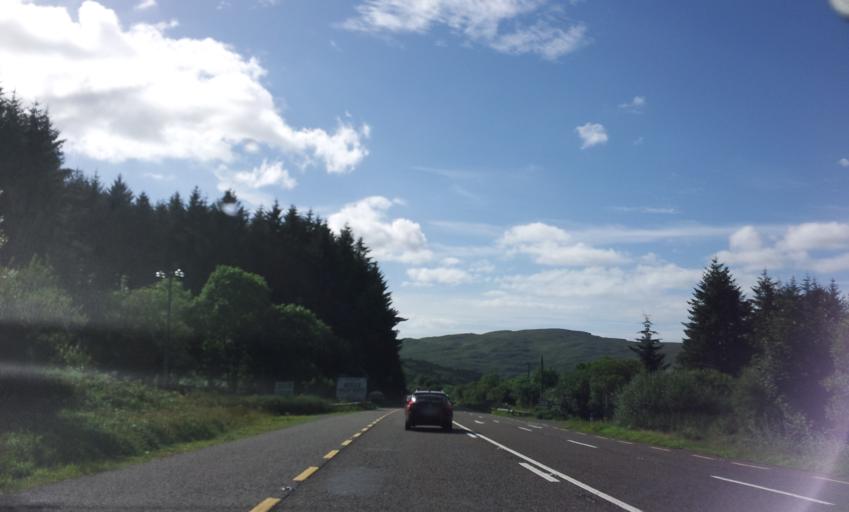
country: IE
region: Munster
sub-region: County Cork
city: Millstreet
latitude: 51.9812
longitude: -9.2639
